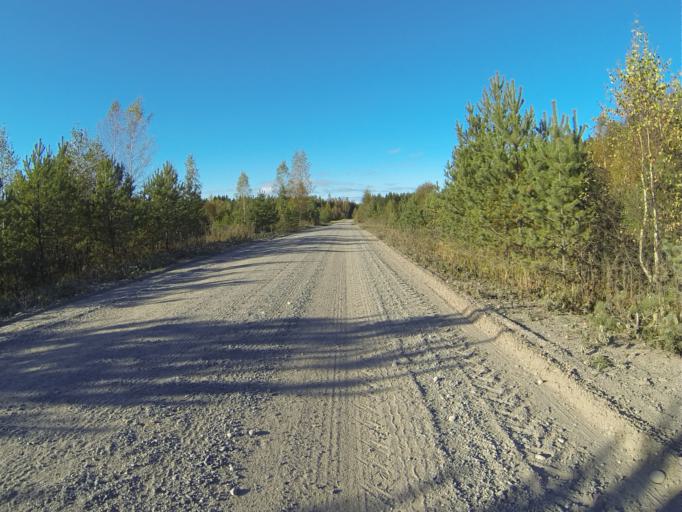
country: FI
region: Varsinais-Suomi
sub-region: Salo
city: Saerkisalo
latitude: 60.2230
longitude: 22.9866
